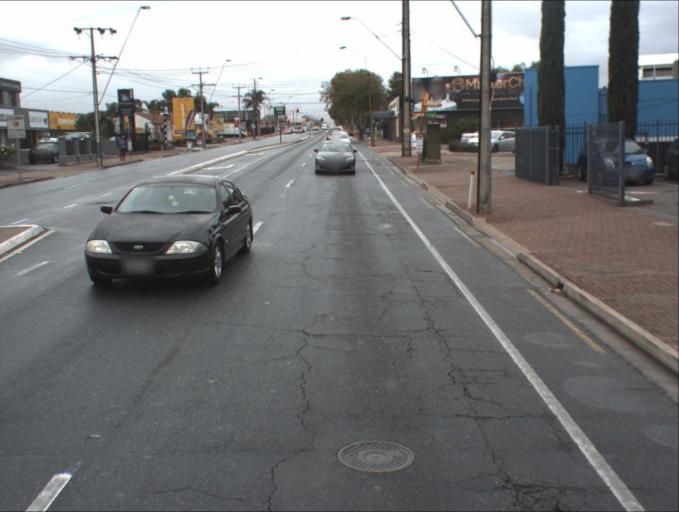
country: AU
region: South Australia
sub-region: Port Adelaide Enfield
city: Klemzig
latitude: -34.8733
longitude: 138.6345
